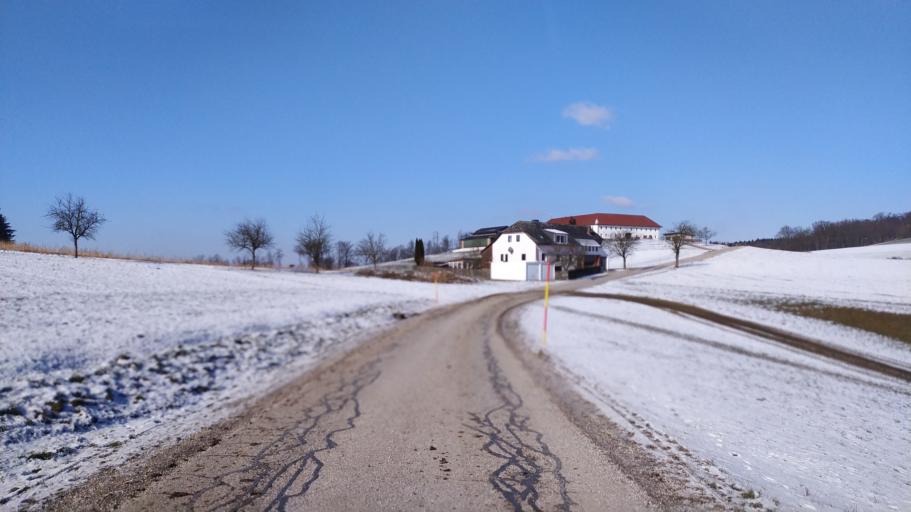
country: AT
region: Upper Austria
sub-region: Politischer Bezirk Urfahr-Umgebung
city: Ottensheim
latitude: 48.3220
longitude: 14.2161
